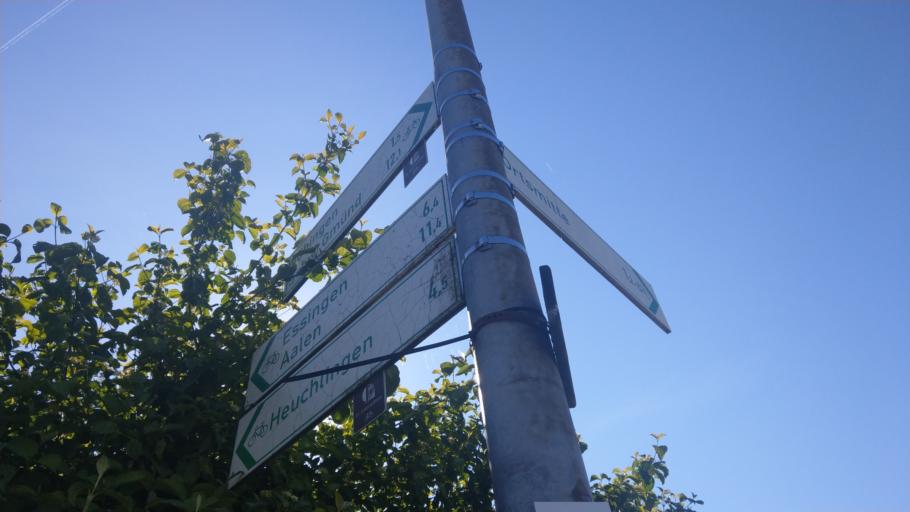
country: DE
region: Baden-Wuerttemberg
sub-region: Regierungsbezirk Stuttgart
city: Mogglingen
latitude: 48.8236
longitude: 9.9537
